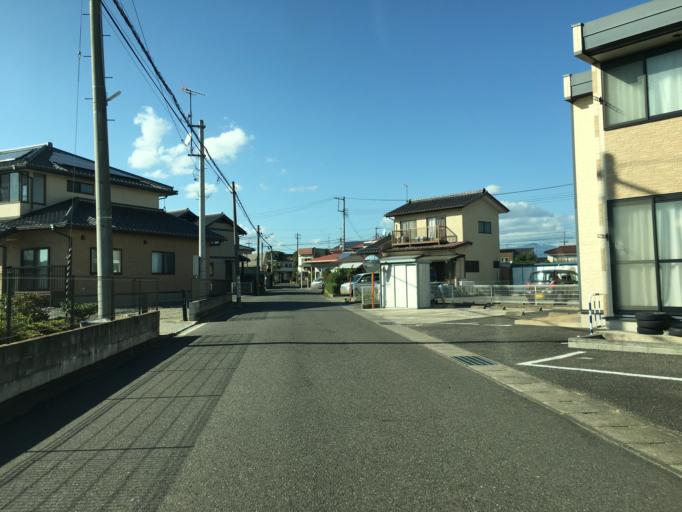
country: JP
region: Fukushima
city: Koriyama
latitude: 37.3875
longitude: 140.3237
